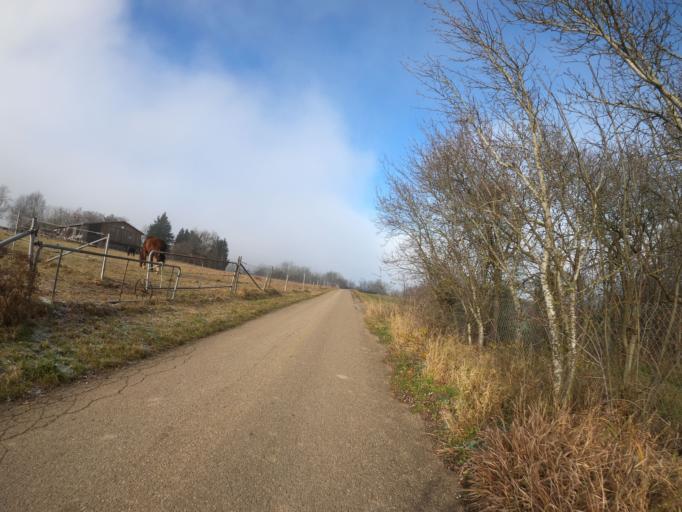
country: DE
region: Baden-Wuerttemberg
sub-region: Regierungsbezirk Stuttgart
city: Bad Uberkingen
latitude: 48.5877
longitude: 9.7578
